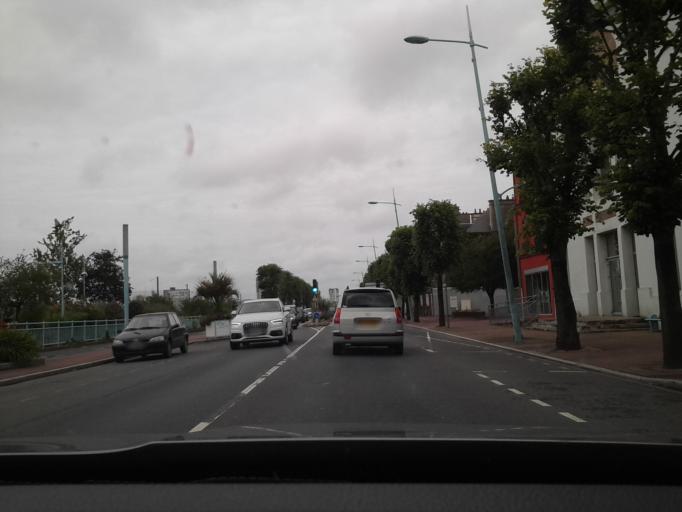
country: FR
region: Lower Normandy
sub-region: Departement de la Manche
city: Cherbourg-Octeville
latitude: 49.6304
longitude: -1.6178
